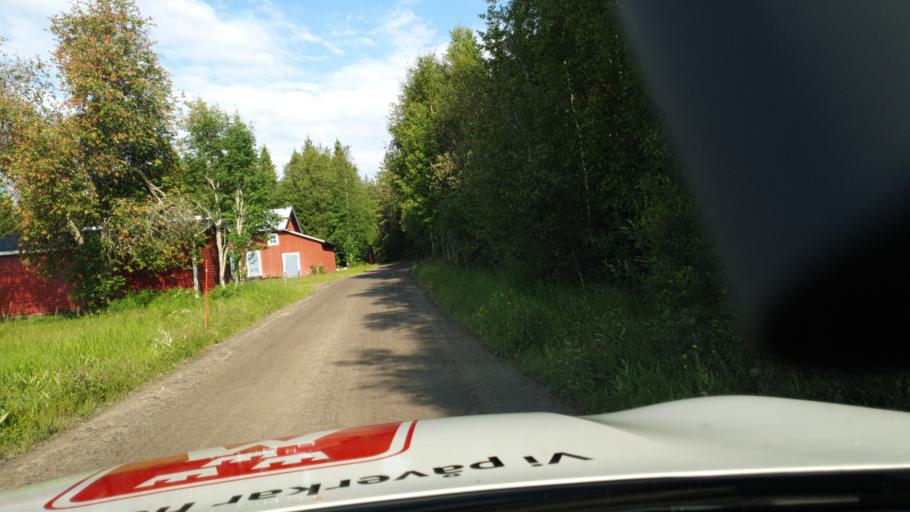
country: SE
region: Vaesterbotten
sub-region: Robertsfors Kommun
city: Robertsfors
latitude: 64.2276
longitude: 21.0561
